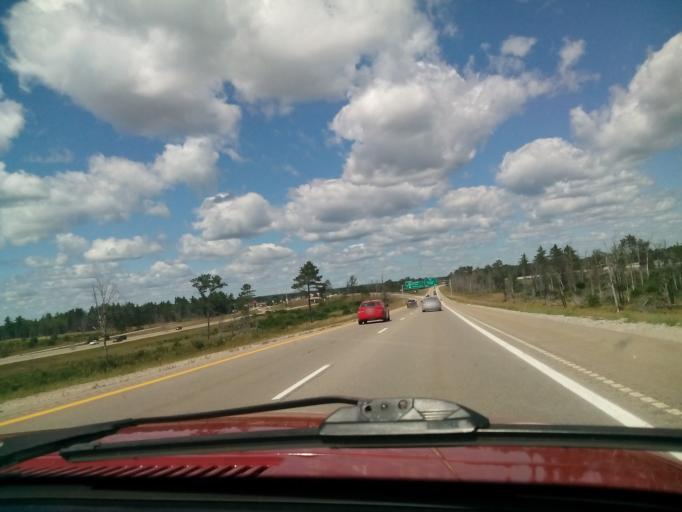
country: US
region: Michigan
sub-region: Crawford County
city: Grayling
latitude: 44.6387
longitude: -84.7077
